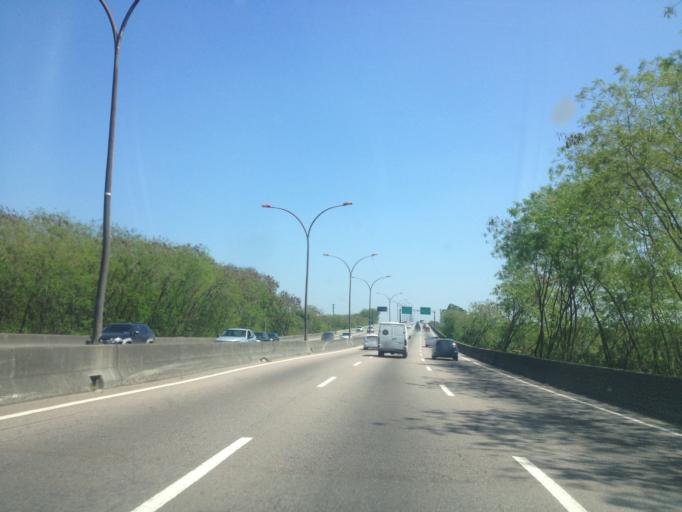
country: BR
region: Rio de Janeiro
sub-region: Duque De Caxias
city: Duque de Caxias
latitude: -22.8030
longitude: -43.3004
